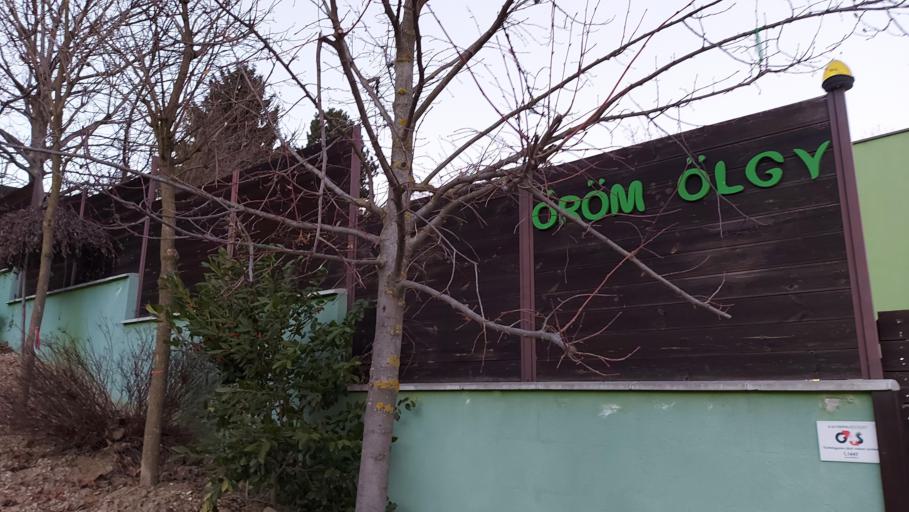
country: HU
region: Pest
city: Budaors
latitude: 47.4661
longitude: 18.9225
